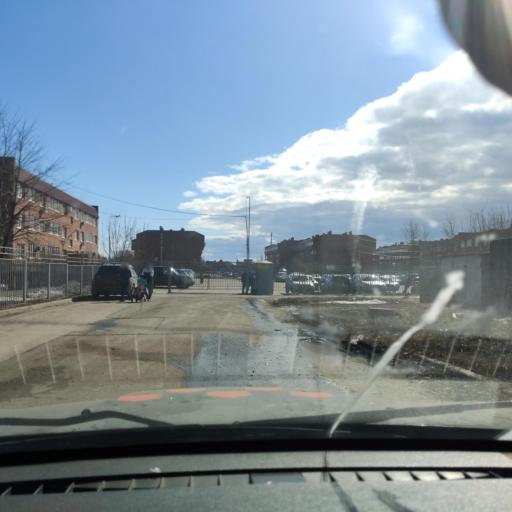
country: RU
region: Samara
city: Podstepki
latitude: 53.5157
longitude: 49.1122
